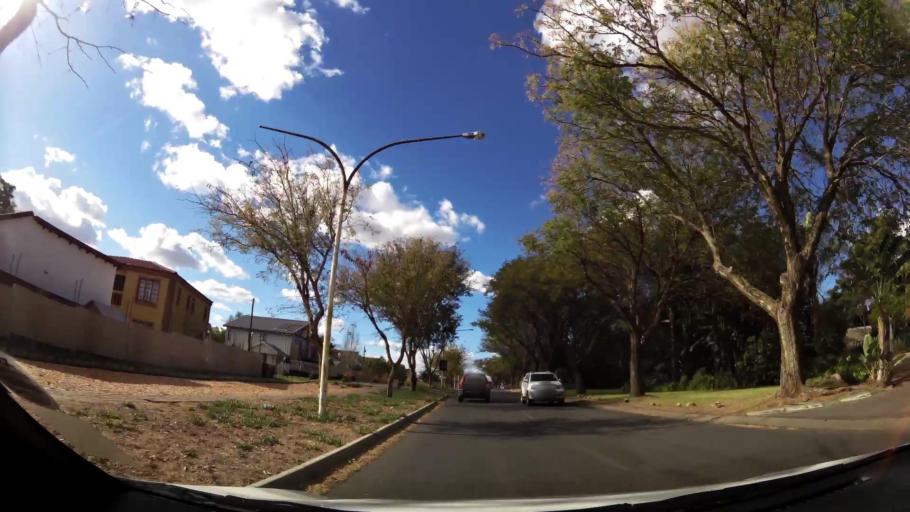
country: ZA
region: Limpopo
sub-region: Capricorn District Municipality
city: Polokwane
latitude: -23.8884
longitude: 29.4797
